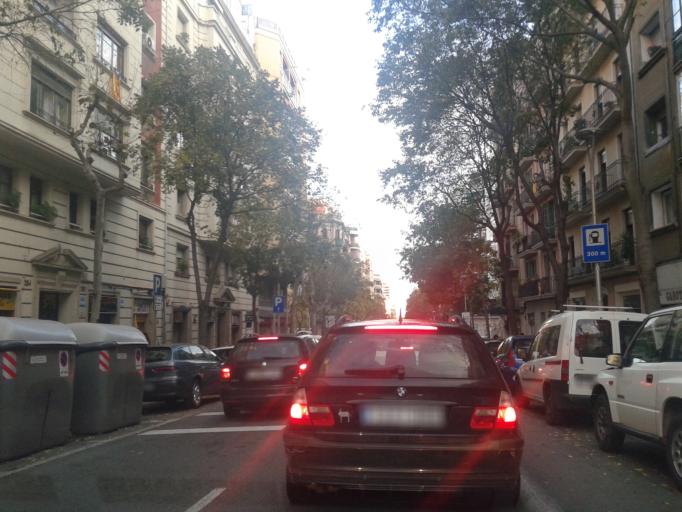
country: ES
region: Catalonia
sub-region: Provincia de Barcelona
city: Horta-Guinardo
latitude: 41.4050
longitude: 2.1760
